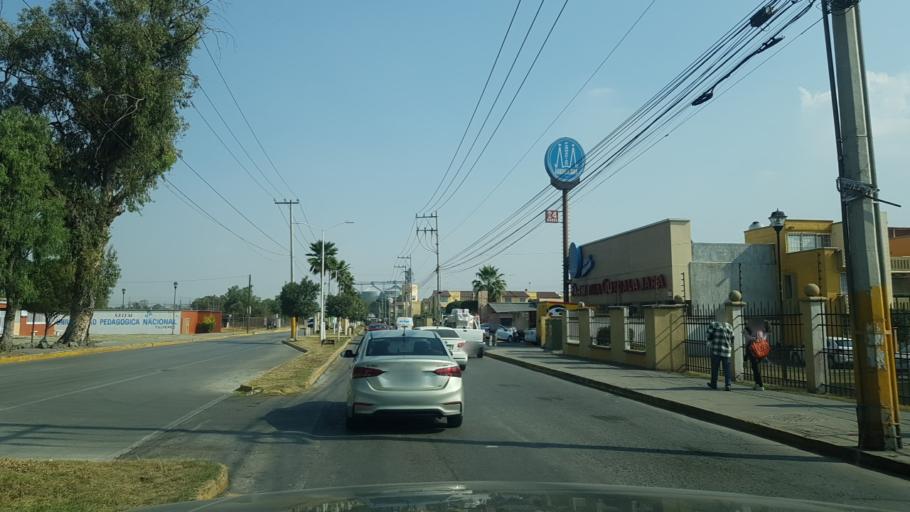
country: MX
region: Mexico
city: Santiago Teyahualco
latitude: 19.6657
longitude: -99.1334
